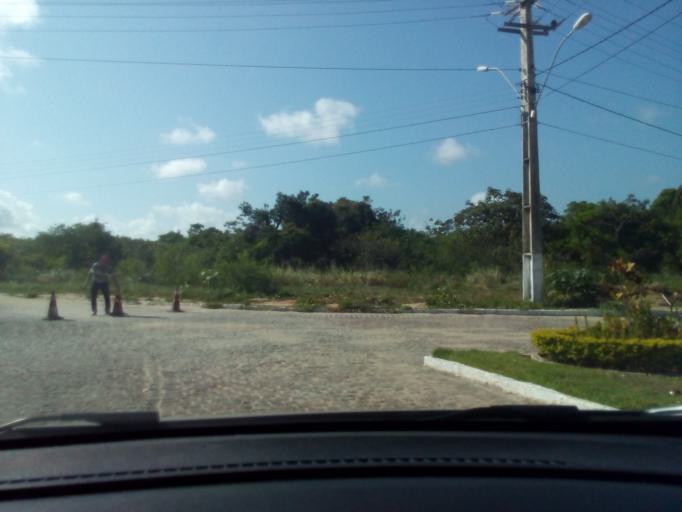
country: BR
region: Rio Grande do Norte
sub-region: Natal
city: Natal
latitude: -5.8379
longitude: -35.2029
